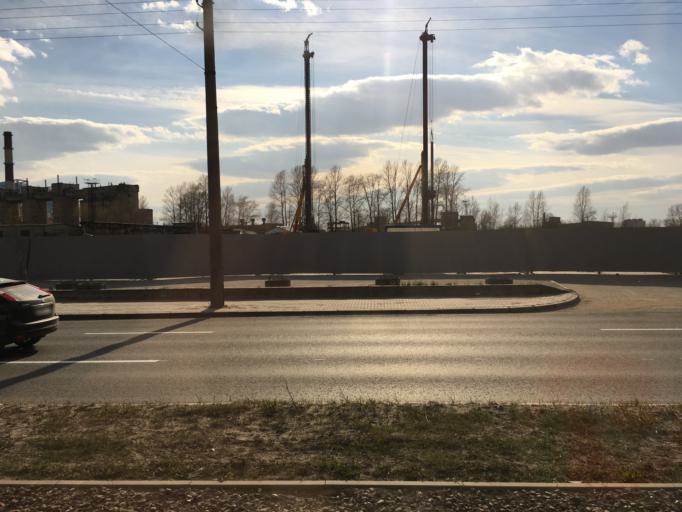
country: RU
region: St.-Petersburg
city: Obukhovo
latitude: 59.8981
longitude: 30.4604
